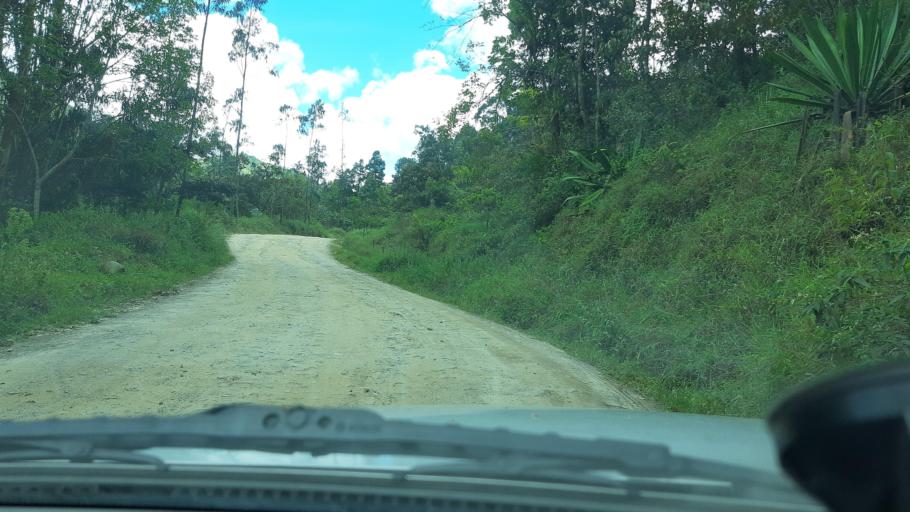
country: CO
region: Cundinamarca
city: Umbita
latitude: 5.2300
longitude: -73.4084
